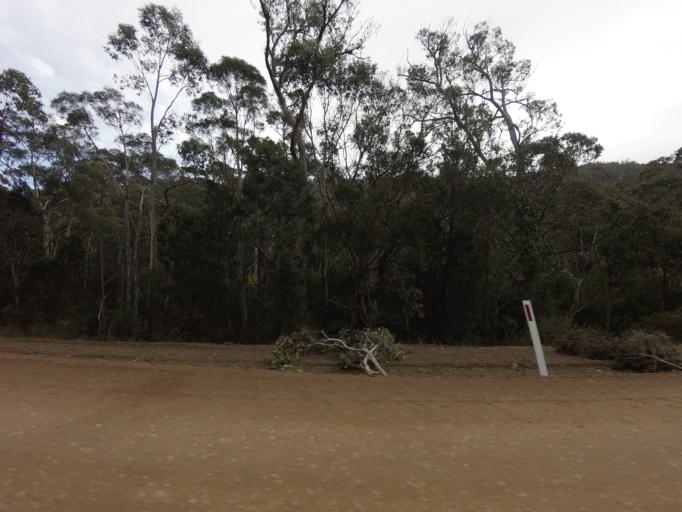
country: AU
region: Tasmania
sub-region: Huon Valley
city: Huonville
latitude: -43.0591
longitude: 147.0953
